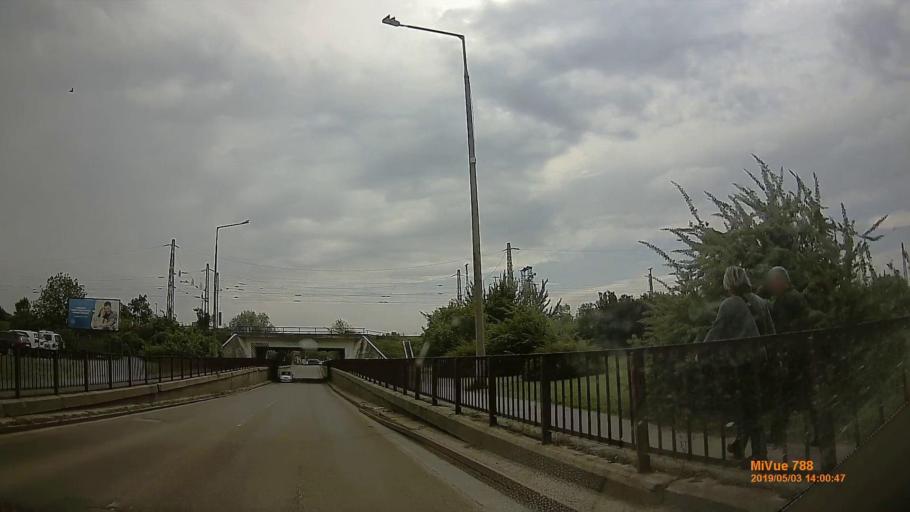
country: HU
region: Jasz-Nagykun-Szolnok
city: Szolnok
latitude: 47.1888
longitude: 20.1946
